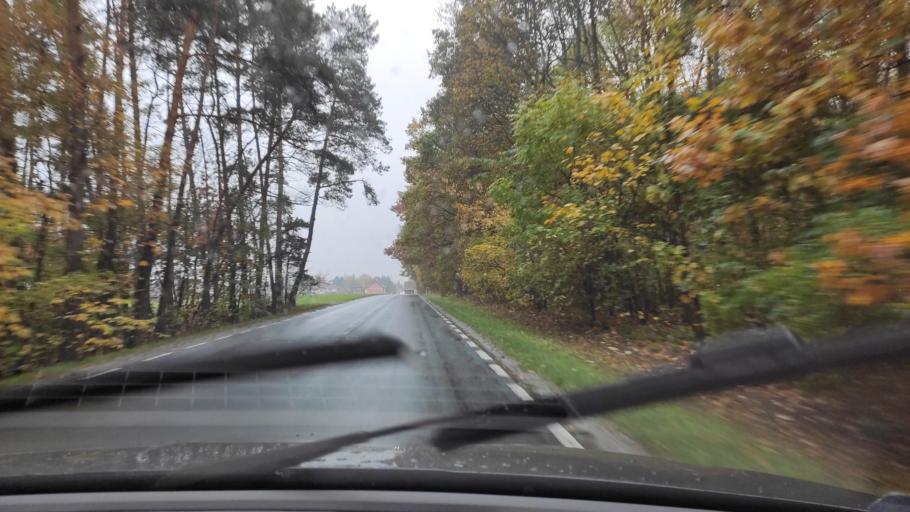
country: PL
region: Greater Poland Voivodeship
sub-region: Powiat poznanski
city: Swarzedz
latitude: 52.3533
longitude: 17.0743
